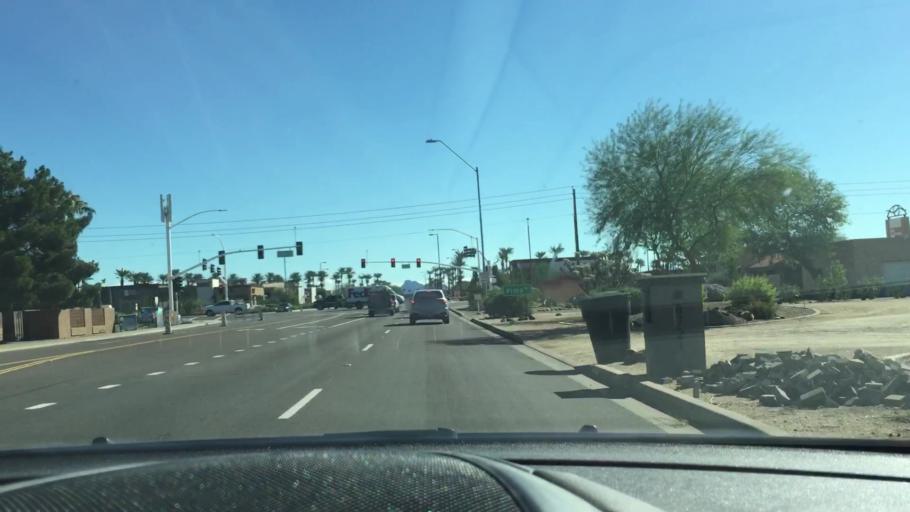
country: US
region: Arizona
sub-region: Maricopa County
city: Scottsdale
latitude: 33.5383
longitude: -111.8926
